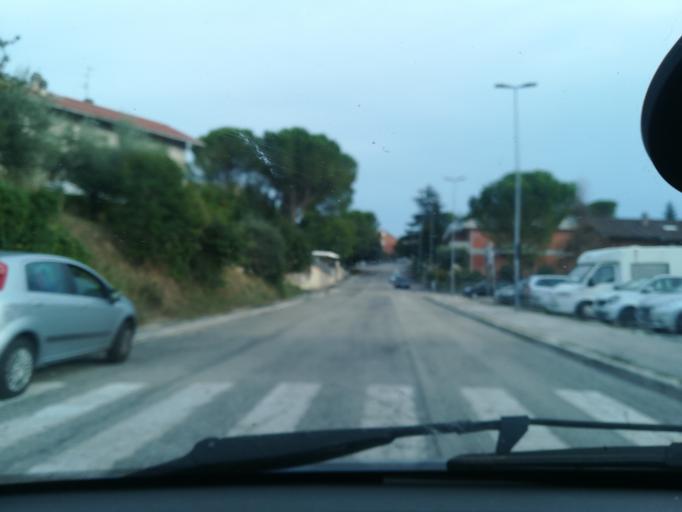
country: IT
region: The Marches
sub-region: Provincia di Macerata
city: Macerata
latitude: 43.3092
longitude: 13.4621
